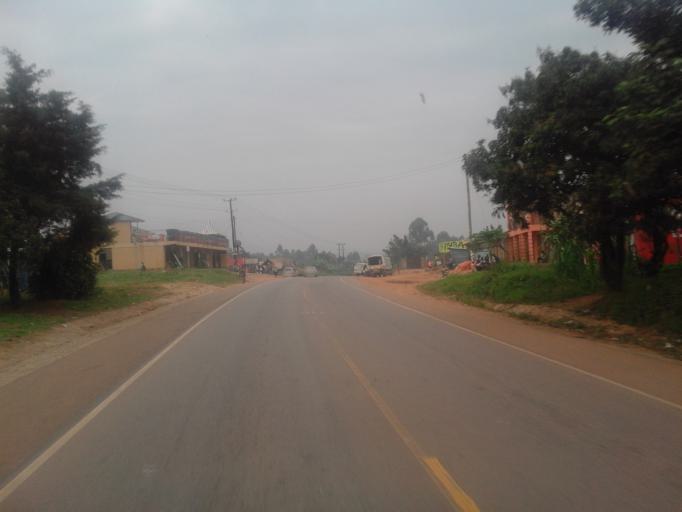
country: UG
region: Central Region
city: Lugazi
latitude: 0.3885
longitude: 32.8440
